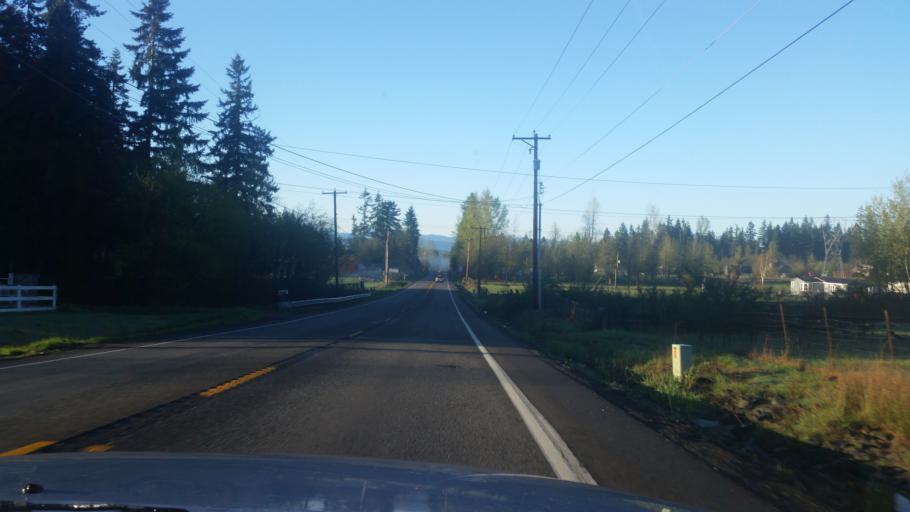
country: US
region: Washington
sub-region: Pierce County
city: Graham
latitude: 47.0223
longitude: -122.2965
